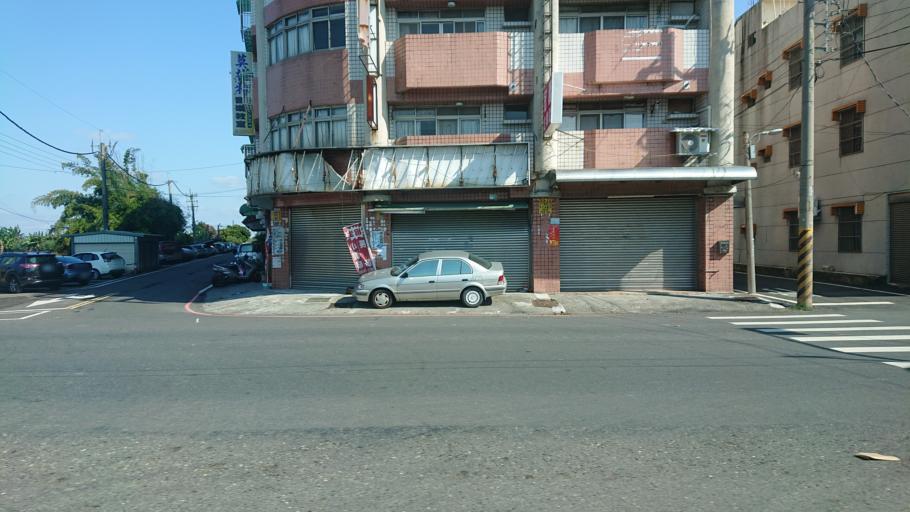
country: TW
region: Taiwan
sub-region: Chiayi
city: Taibao
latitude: 23.4346
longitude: 120.3943
